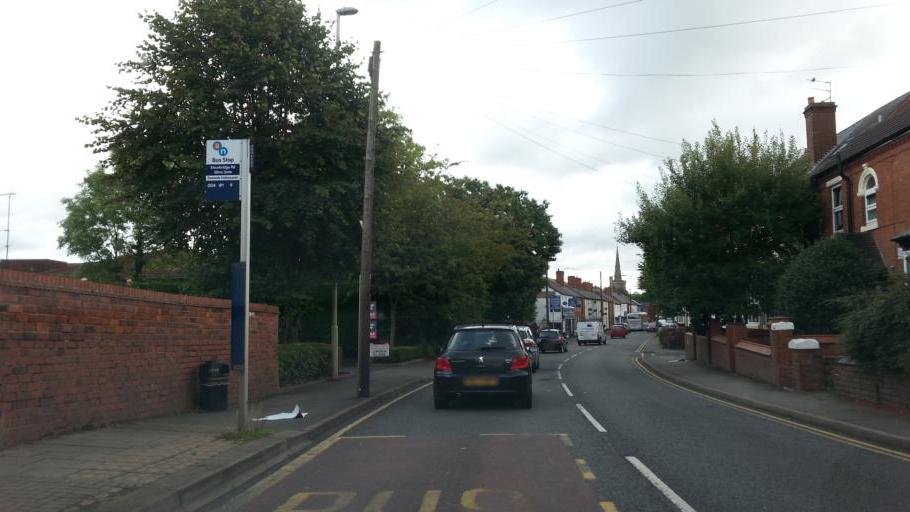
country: GB
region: England
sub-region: Dudley
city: Halesowen
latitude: 52.4524
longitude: -2.0563
